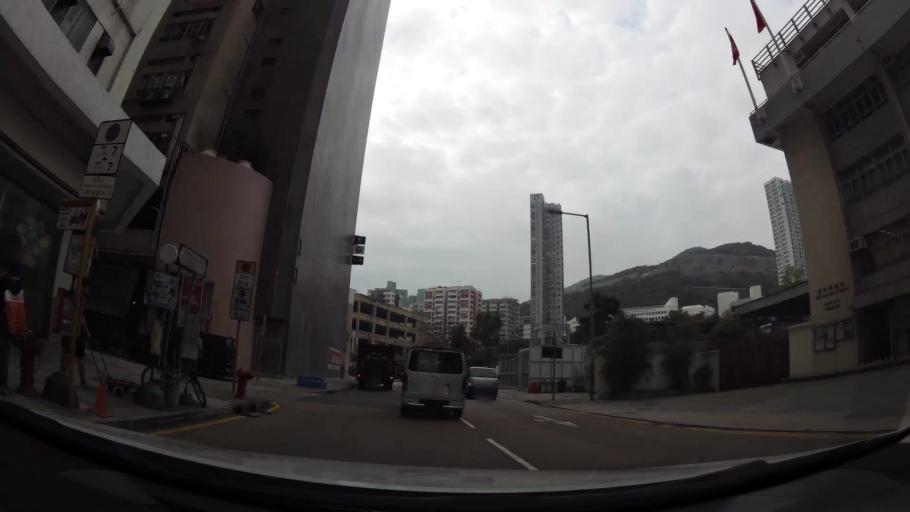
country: HK
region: Wanchai
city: Wan Chai
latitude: 22.2673
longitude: 114.2436
